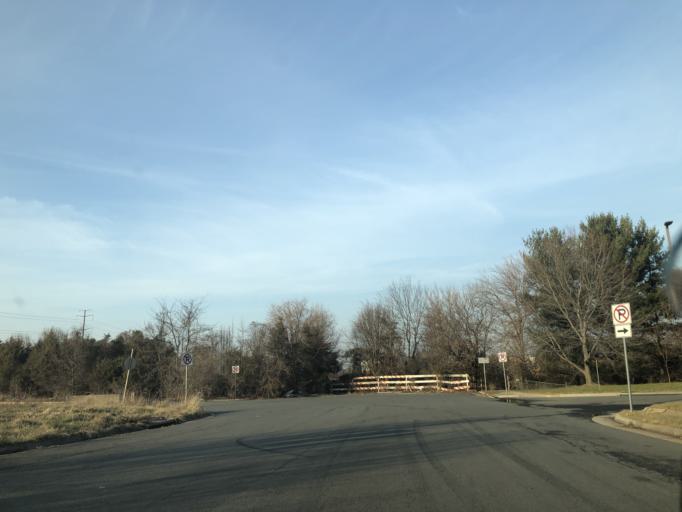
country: US
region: Virginia
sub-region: Fairfax County
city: Floris
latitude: 38.9404
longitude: -77.4277
